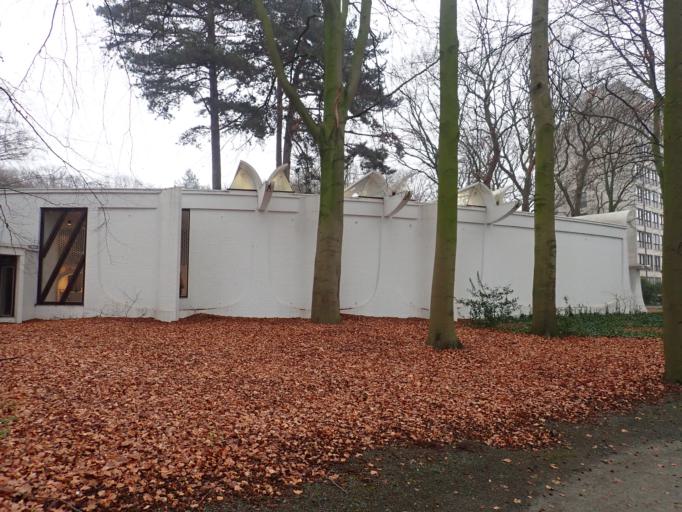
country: BE
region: Flanders
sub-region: Provincie Antwerpen
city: Edegem
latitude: 51.1787
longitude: 4.4130
